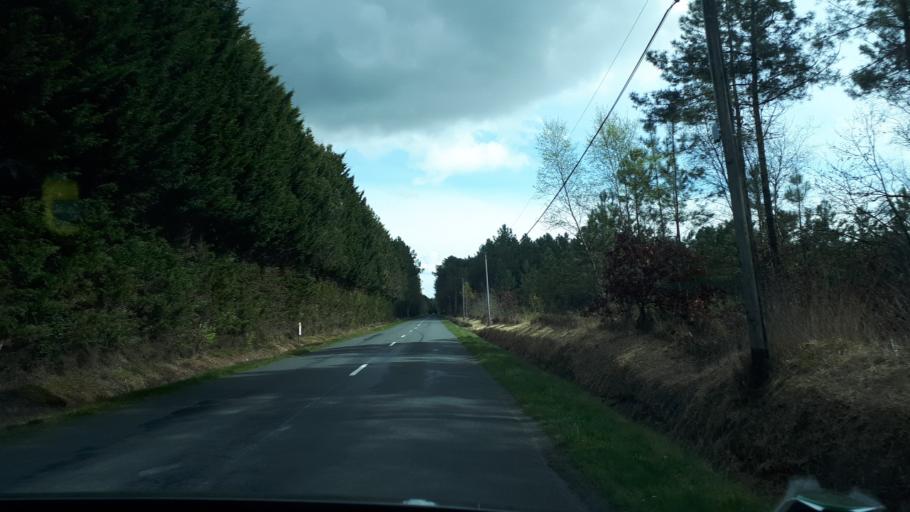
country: FR
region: Pays de la Loire
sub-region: Departement de la Sarthe
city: Challes
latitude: 47.8740
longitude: 0.4128
